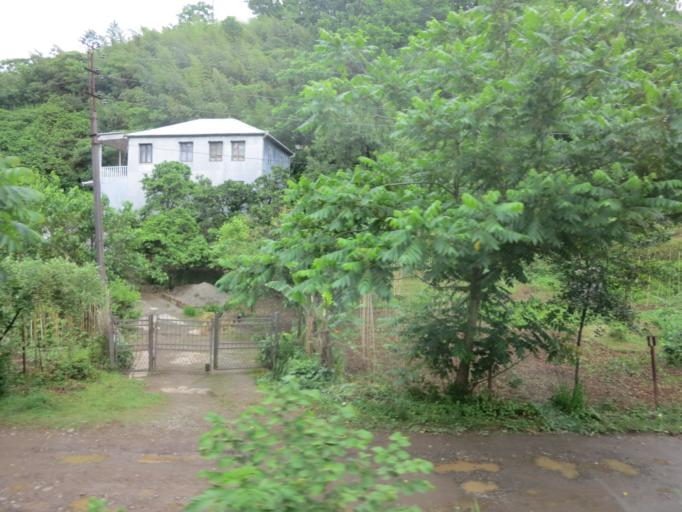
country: GE
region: Ajaria
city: Kobuleti
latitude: 41.7770
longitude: 41.7615
